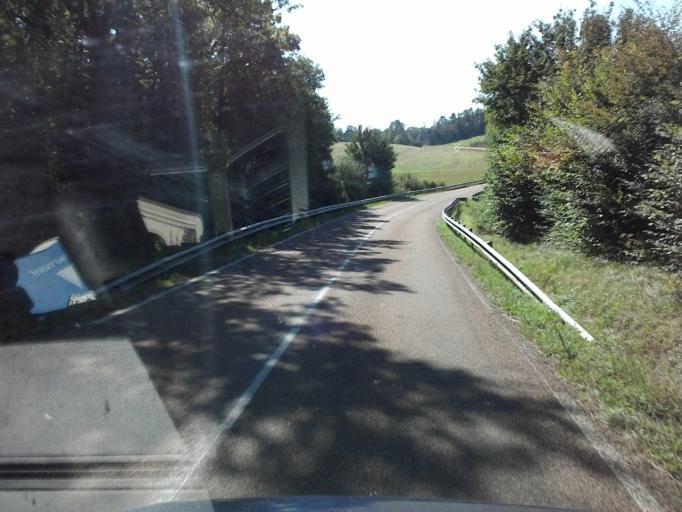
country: FR
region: Bourgogne
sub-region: Departement de l'Yonne
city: Joux-la-Ville
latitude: 47.7006
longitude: 3.8983
